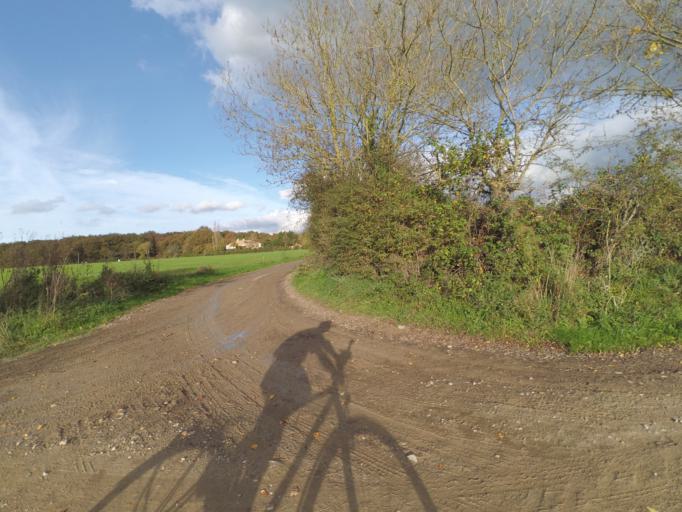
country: FR
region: Pays de la Loire
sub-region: Departement de la Vendee
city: Saint-Hilaire-de-Loulay
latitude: 47.0134
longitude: -1.3487
